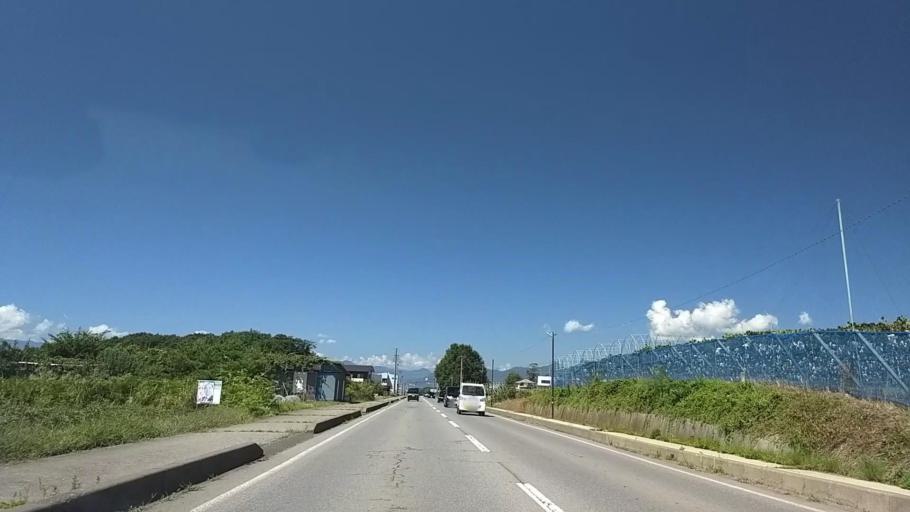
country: JP
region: Nagano
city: Komoro
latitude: 36.3601
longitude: 138.3631
